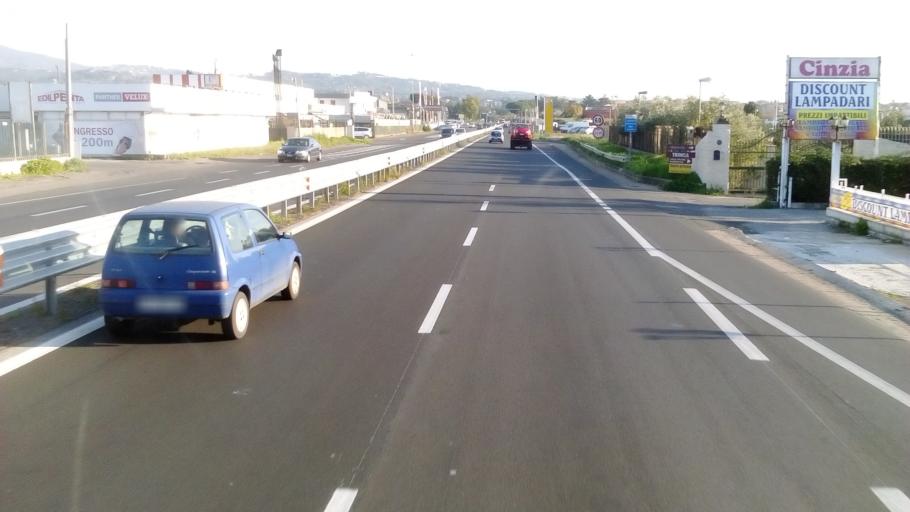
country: IT
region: Latium
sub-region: Citta metropolitana di Roma Capitale
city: Ciampino
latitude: 41.7850
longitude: 12.5992
